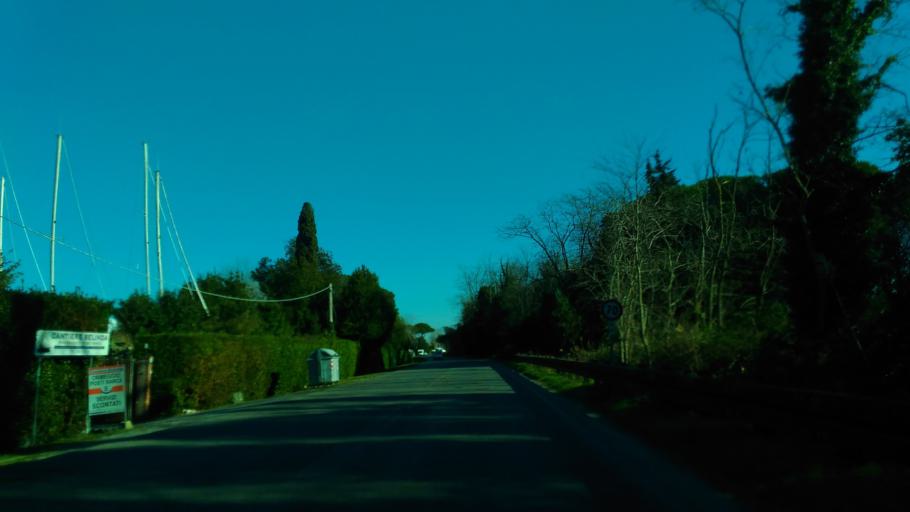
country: IT
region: Tuscany
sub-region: Province of Pisa
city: Marina di Pisa
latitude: 43.6768
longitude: 10.3064
